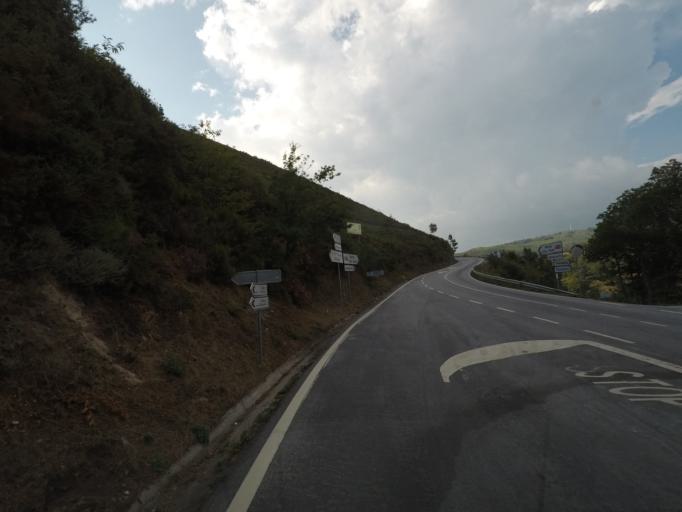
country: PT
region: Porto
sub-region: Baiao
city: Valadares
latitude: 41.1826
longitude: -7.9373
